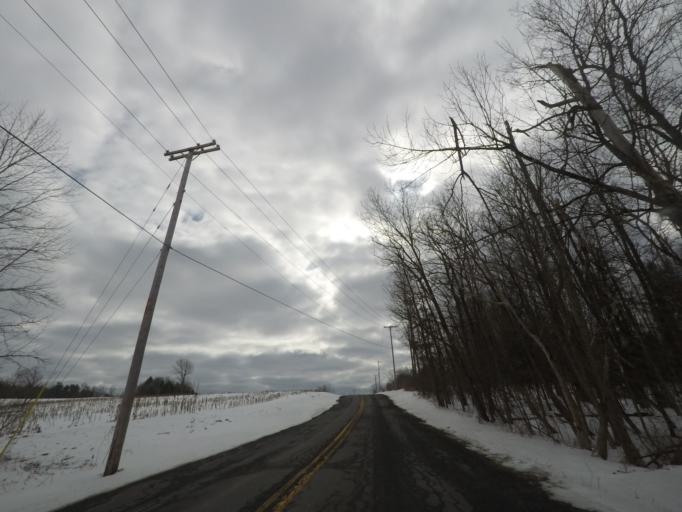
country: US
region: New York
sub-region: Rensselaer County
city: Hoosick Falls
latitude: 42.9410
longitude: -73.4321
